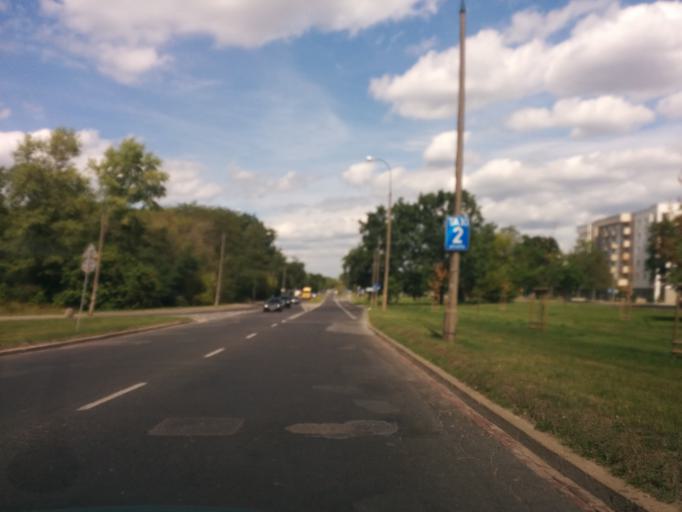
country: PL
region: Masovian Voivodeship
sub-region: Warszawa
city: Bialoleka
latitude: 52.3148
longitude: 21.0007
